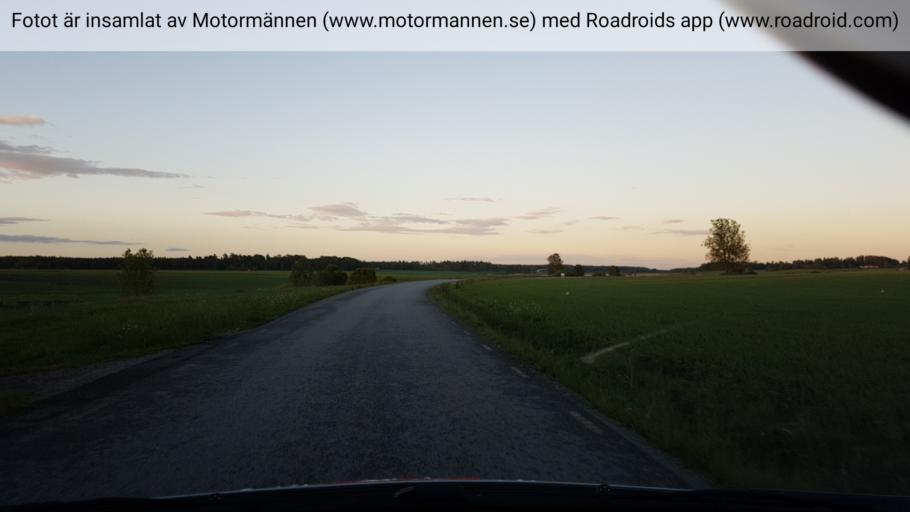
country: SE
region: Vaestmanland
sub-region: Vasteras
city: Skultuna
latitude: 59.7058
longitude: 16.4579
